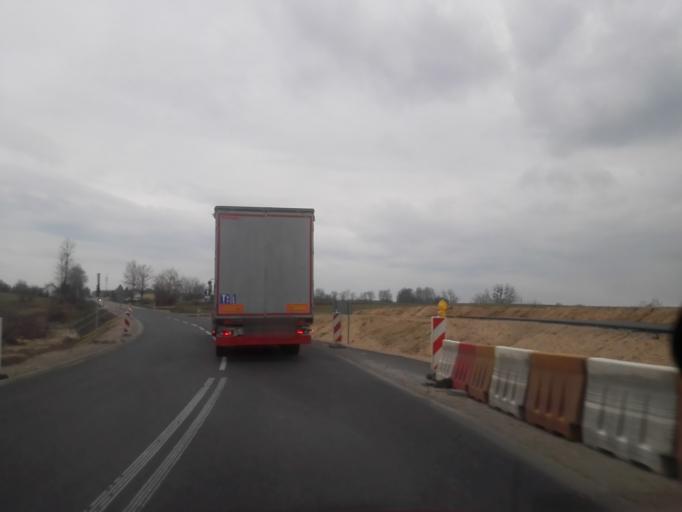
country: PL
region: Podlasie
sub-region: Powiat grajewski
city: Rajgrod
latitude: 53.7786
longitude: 22.8355
